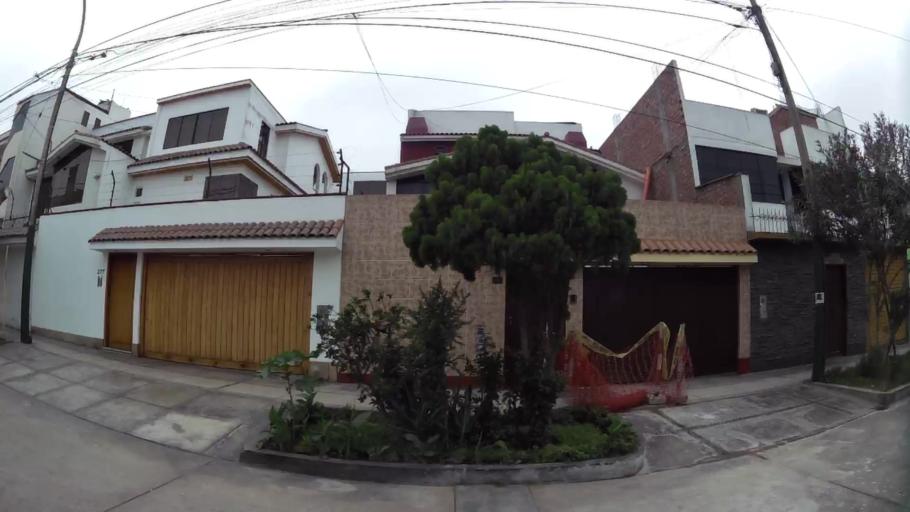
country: PE
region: Lima
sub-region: Lima
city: Surco
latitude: -12.1352
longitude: -76.9849
